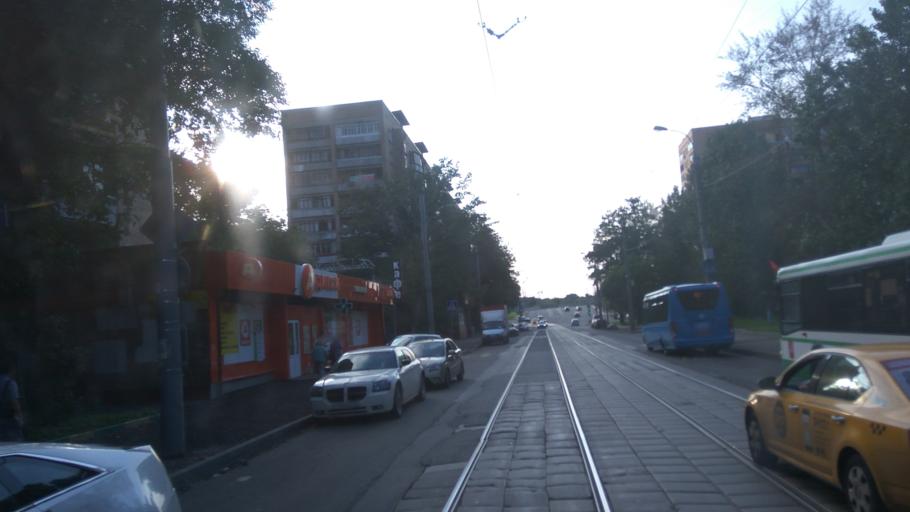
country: RU
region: Moskovskaya
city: Koptevo
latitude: 55.8393
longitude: 37.5281
